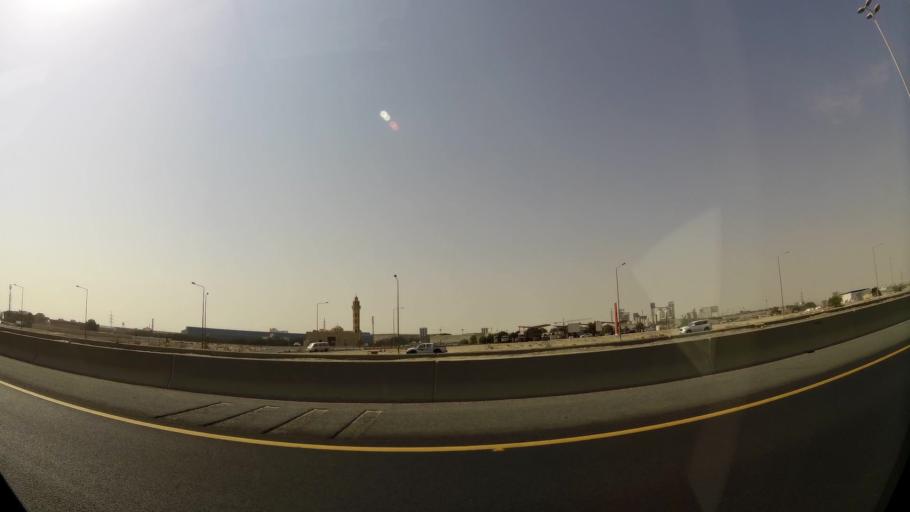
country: KW
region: Al Ahmadi
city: Al Fahahil
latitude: 29.0034
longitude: 48.1375
